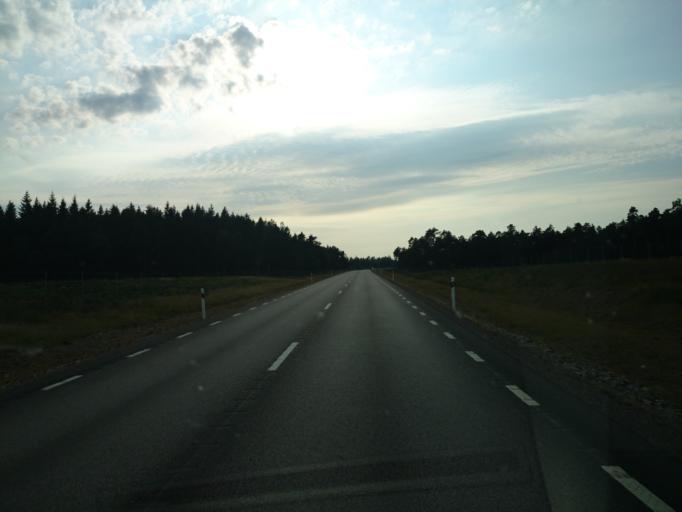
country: SE
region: Kronoberg
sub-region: Markaryds Kommun
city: Stromsnasbruk
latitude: 56.4457
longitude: 13.8167
